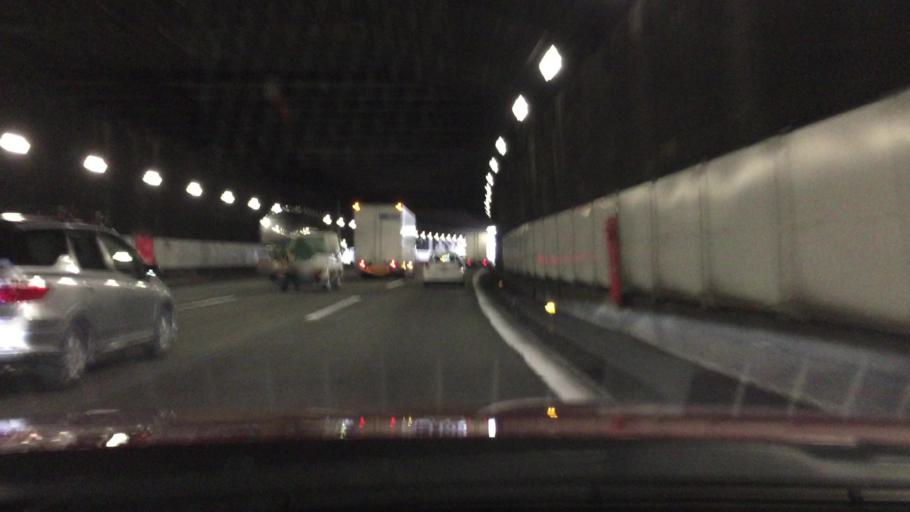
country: JP
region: Hyogo
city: Takarazuka
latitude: 34.8218
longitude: 135.3215
